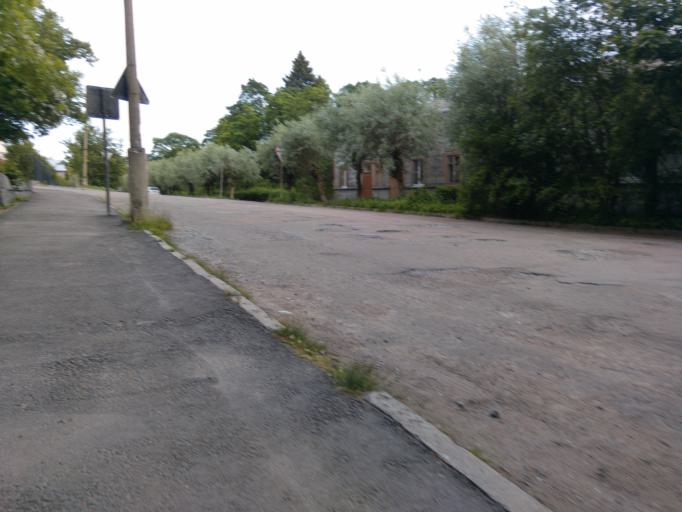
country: RU
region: Republic of Karelia
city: Sortavala
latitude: 61.7046
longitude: 30.6856
